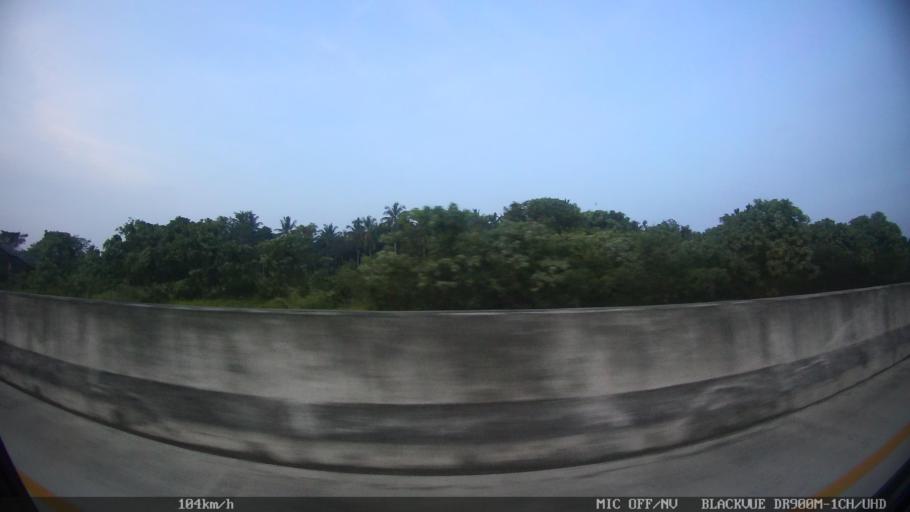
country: ID
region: Lampung
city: Kalianda
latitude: -5.6979
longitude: 105.6284
